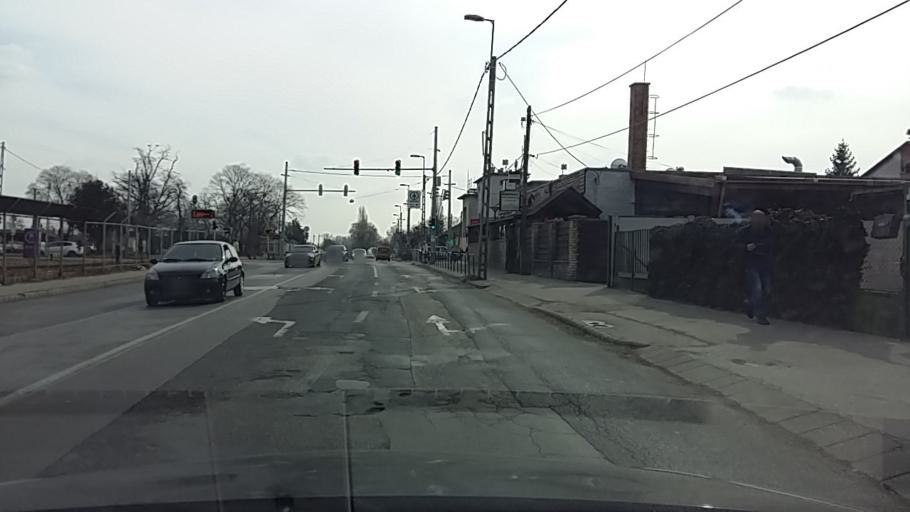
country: HU
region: Budapest
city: Budapest XVIII. keruelet
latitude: 47.4043
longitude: 19.1855
